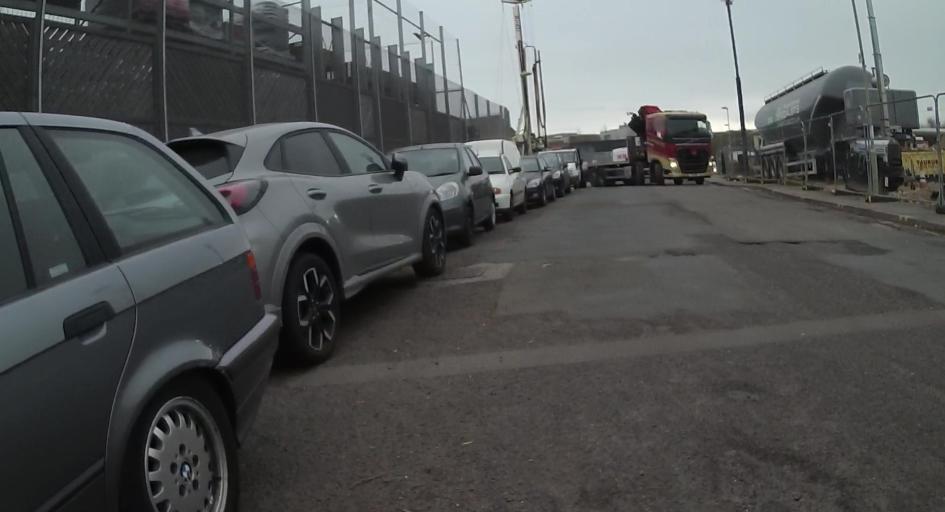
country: GB
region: England
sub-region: Hampshire
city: Farnborough
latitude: 51.2883
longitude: -0.7640
